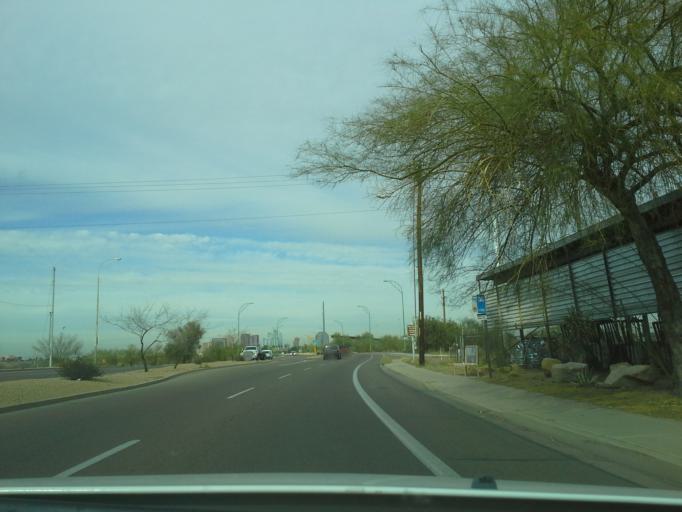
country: US
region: Arizona
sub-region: Maricopa County
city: Phoenix
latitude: 33.4176
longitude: -112.0735
